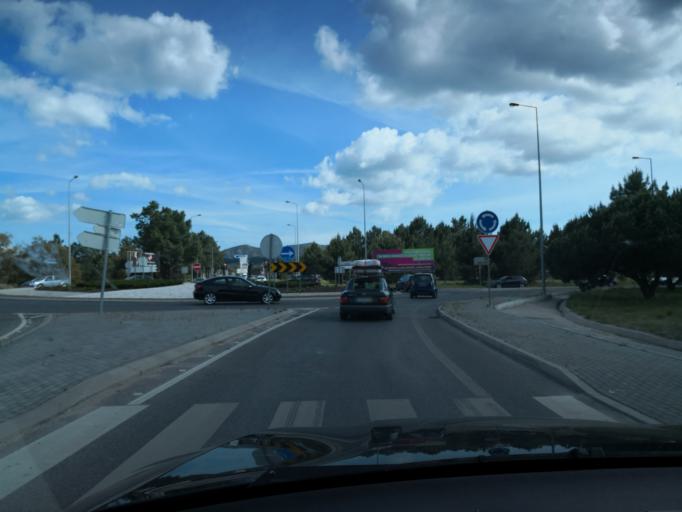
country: PT
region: Setubal
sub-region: Palmela
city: Quinta do Anjo
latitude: 38.5327
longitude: -9.0221
